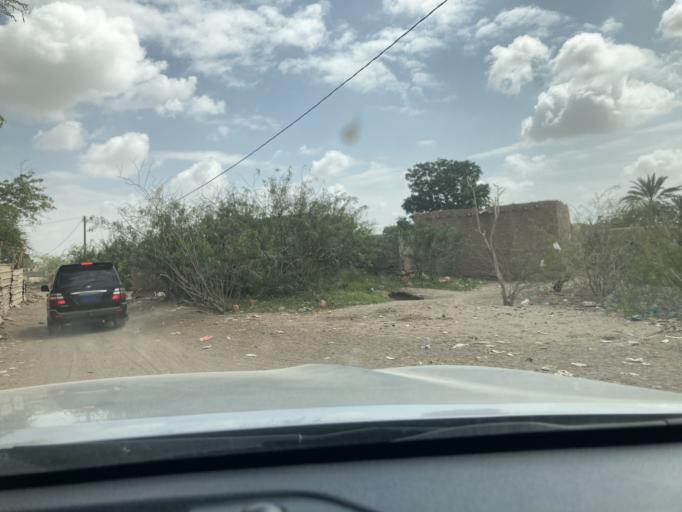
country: YE
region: Lahij
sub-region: Al  Hawtah
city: Lahij
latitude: 13.0168
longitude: 45.0038
